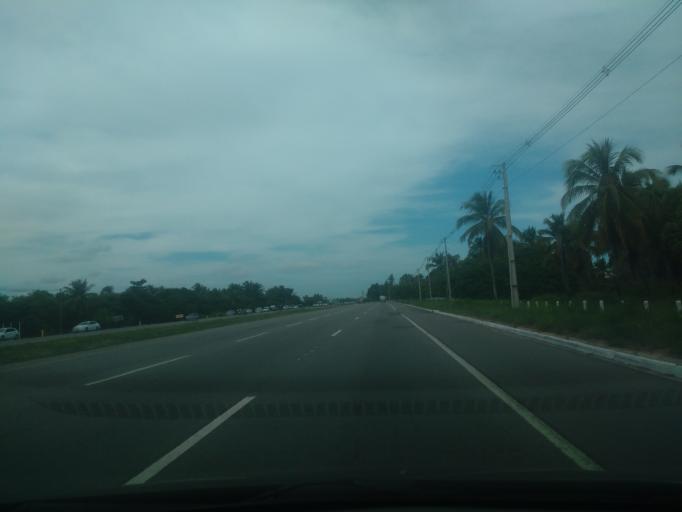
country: BR
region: Alagoas
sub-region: Maceio
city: Maceio
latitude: -9.7047
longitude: -35.8078
